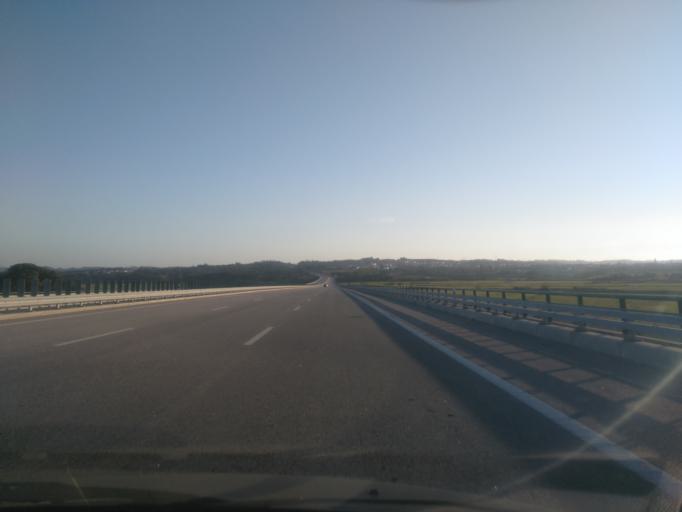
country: PT
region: Coimbra
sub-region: Figueira da Foz
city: Lavos
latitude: 40.1021
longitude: -8.7482
